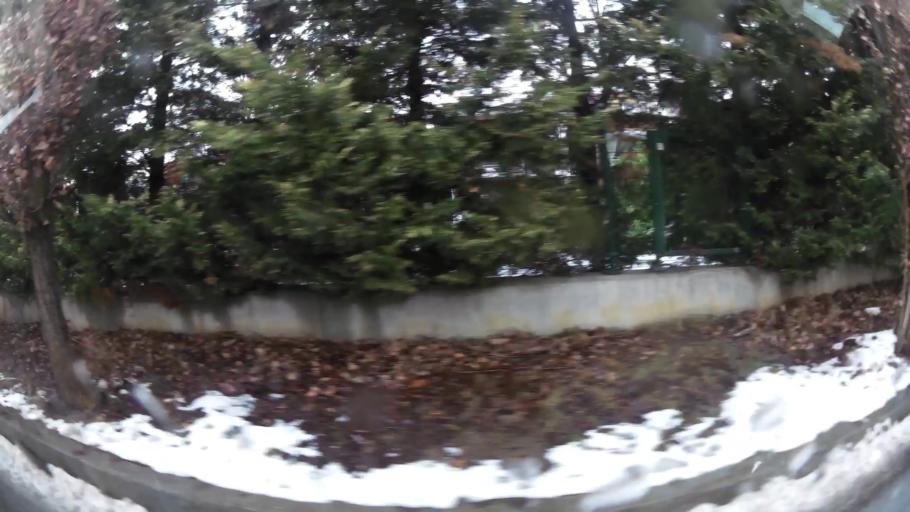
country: BG
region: Sofia-Capital
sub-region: Stolichna Obshtina
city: Sofia
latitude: 42.6585
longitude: 23.2770
